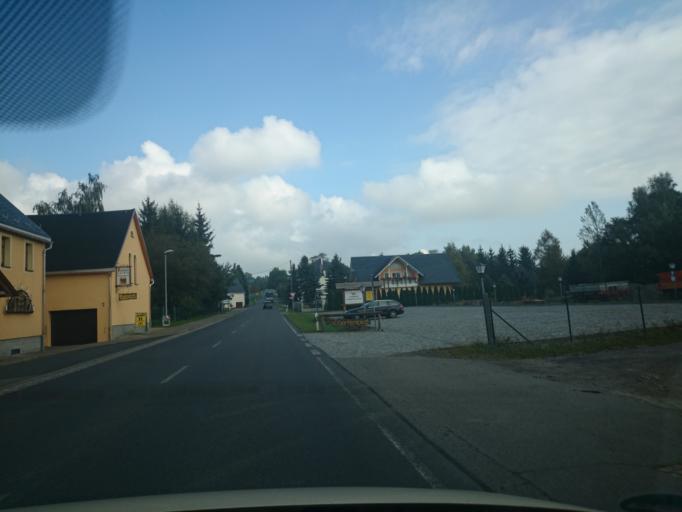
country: DE
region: Saxony
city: Grosshartmannsdorf
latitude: 50.8064
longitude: 13.3232
